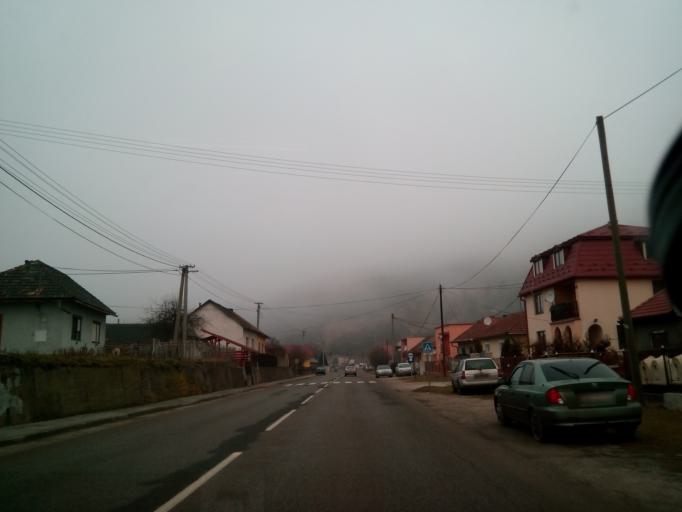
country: SK
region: Kosicky
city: Krompachy
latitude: 48.9252
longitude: 20.8579
